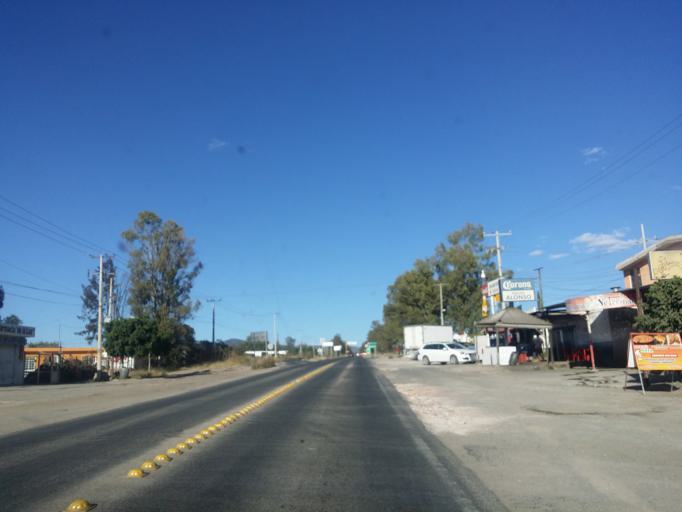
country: MX
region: Guanajuato
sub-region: Silao de la Victoria
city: El Refugio de los Sauces
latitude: 21.0264
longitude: -101.5357
